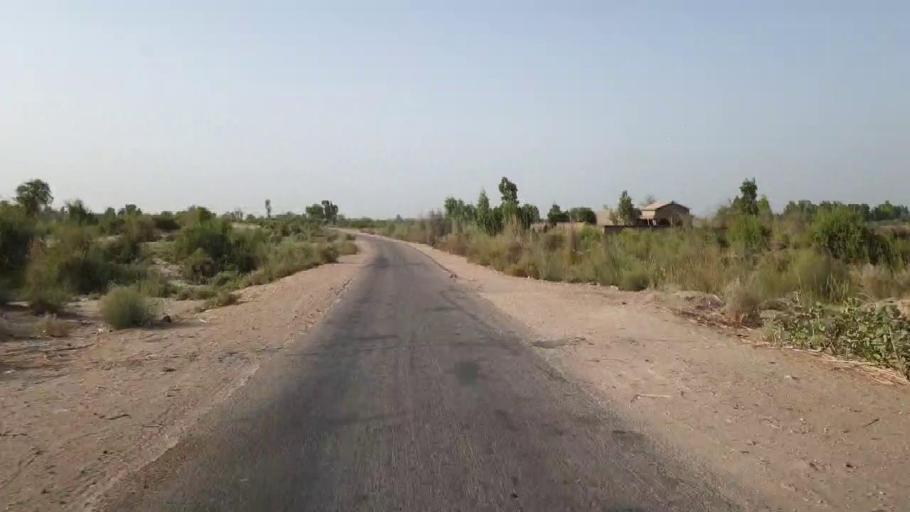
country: PK
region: Sindh
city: Jam Sahib
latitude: 26.4847
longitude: 68.8606
